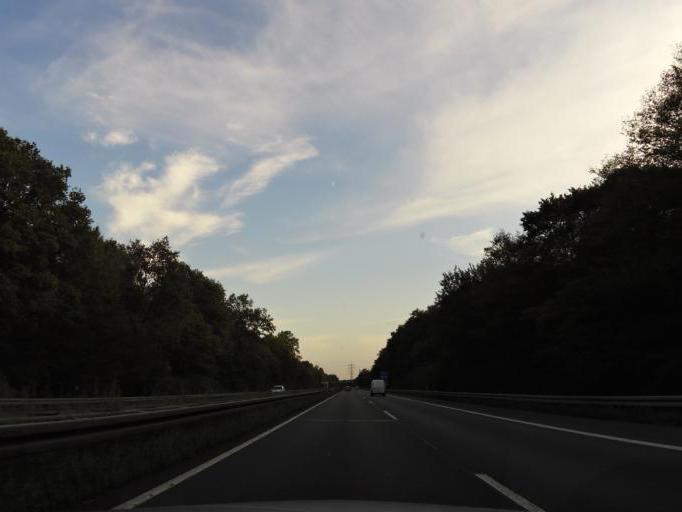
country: DE
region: Hesse
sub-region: Regierungsbezirk Darmstadt
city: Alsbach-Hahnlein
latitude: 49.7343
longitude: 8.5430
